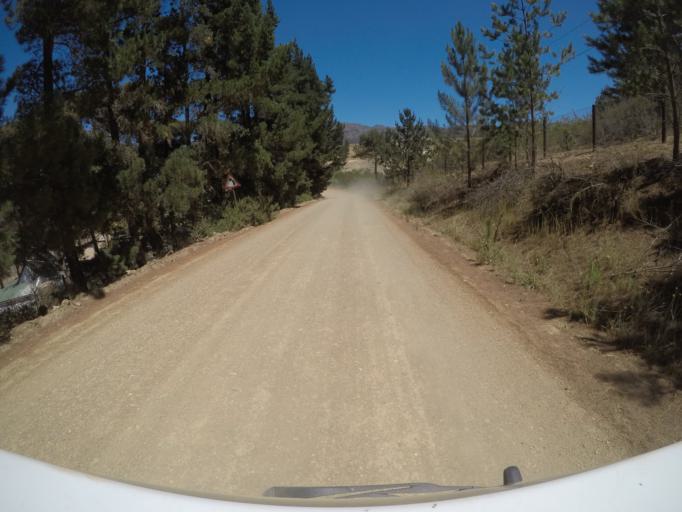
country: ZA
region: Western Cape
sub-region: Overberg District Municipality
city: Caledon
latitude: -34.1746
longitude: 19.2268
